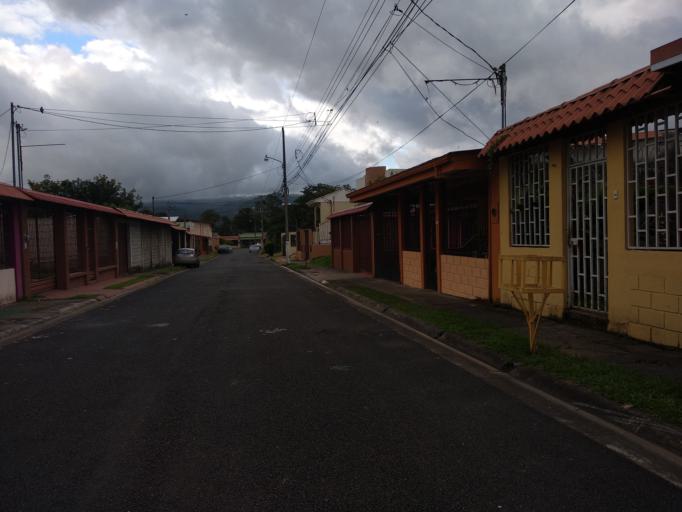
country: CR
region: Cartago
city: Turrialba
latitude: 9.8991
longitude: -83.6740
